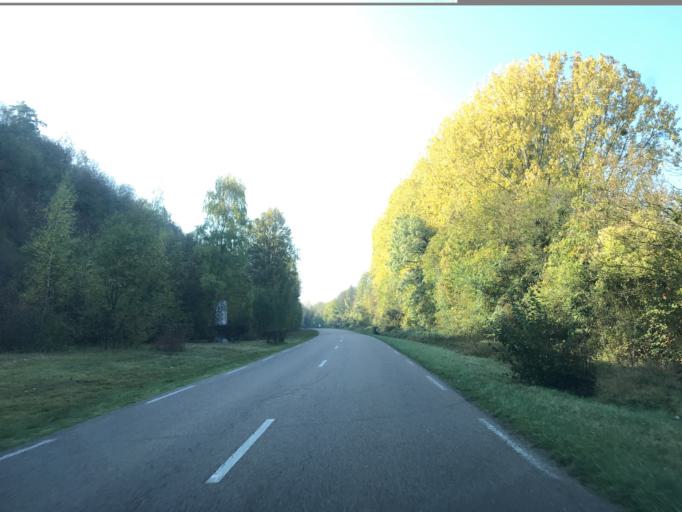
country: FR
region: Haute-Normandie
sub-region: Departement de l'Eure
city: Le Vaudreuil
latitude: 49.2390
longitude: 1.1913
